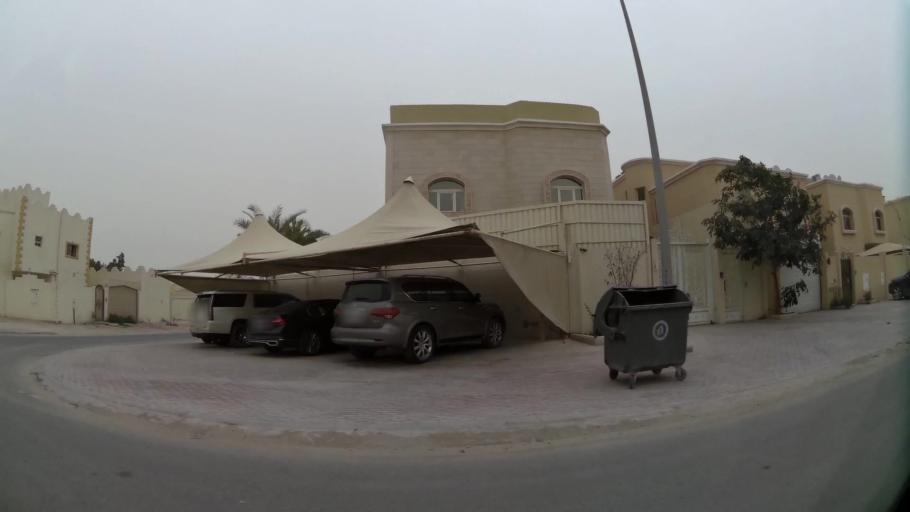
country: QA
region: Baladiyat ad Dawhah
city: Doha
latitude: 25.2433
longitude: 51.4881
